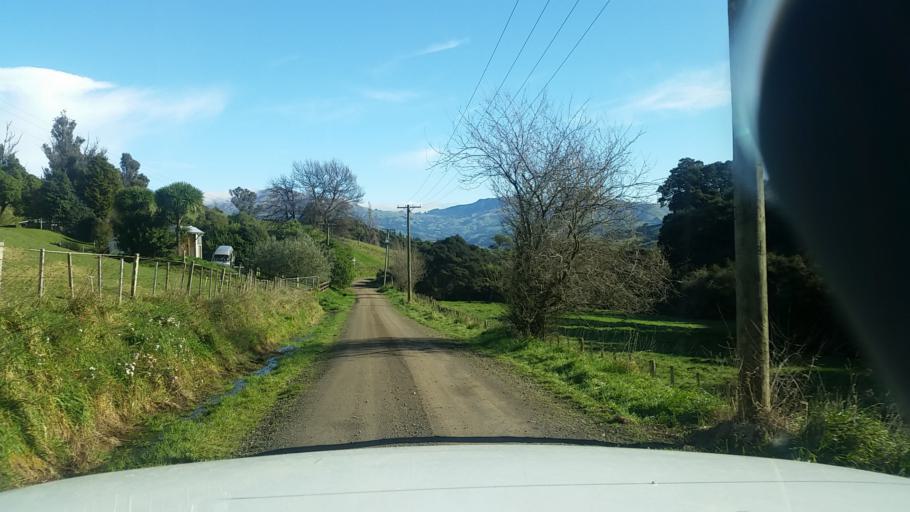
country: NZ
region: Canterbury
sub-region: Christchurch City
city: Christchurch
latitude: -43.7904
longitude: 172.9881
